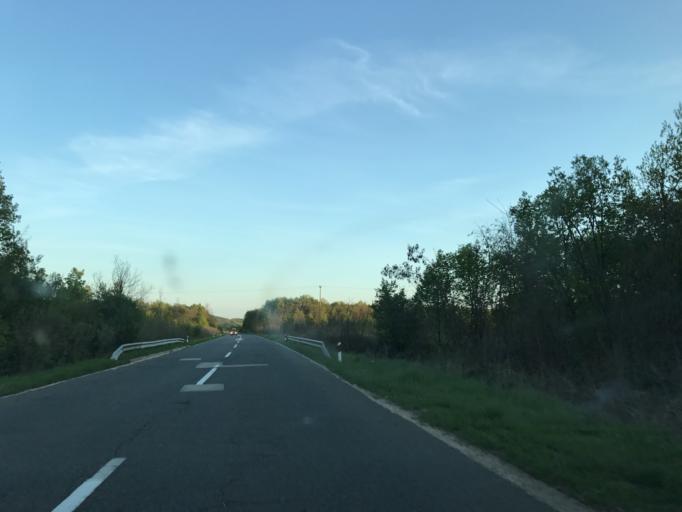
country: RO
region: Mehedinti
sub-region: Comuna Gogosu
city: Ostrovu Mare
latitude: 44.4457
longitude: 22.4546
